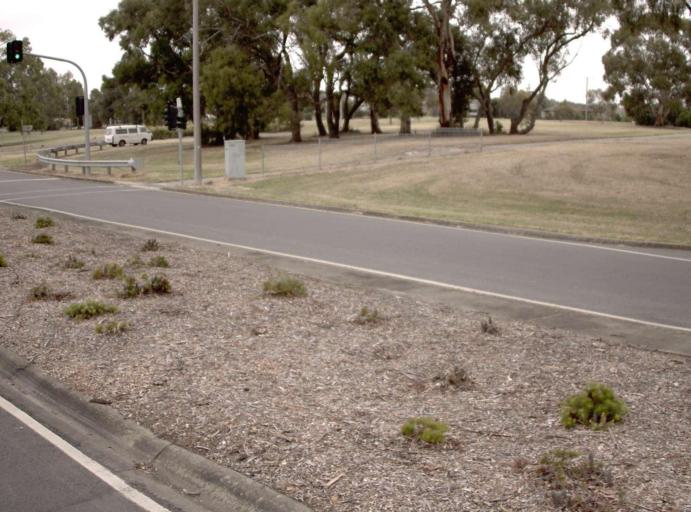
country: AU
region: Victoria
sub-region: Latrobe
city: Morwell
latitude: -38.3076
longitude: 146.4209
